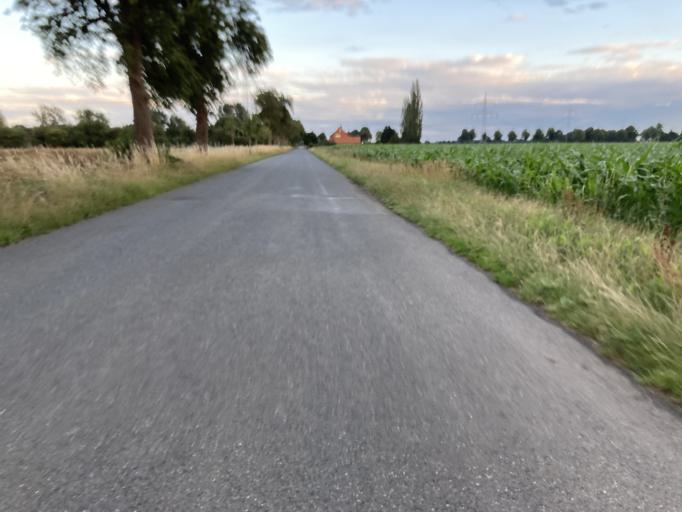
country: DE
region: Lower Saxony
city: Verden
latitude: 52.9261
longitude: 9.2007
